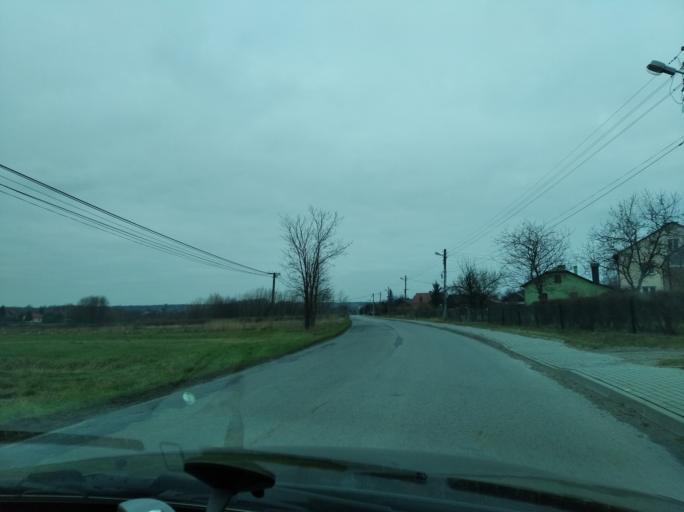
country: PL
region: Subcarpathian Voivodeship
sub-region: Powiat lancucki
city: Rakszawa
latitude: 50.1621
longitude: 22.2380
